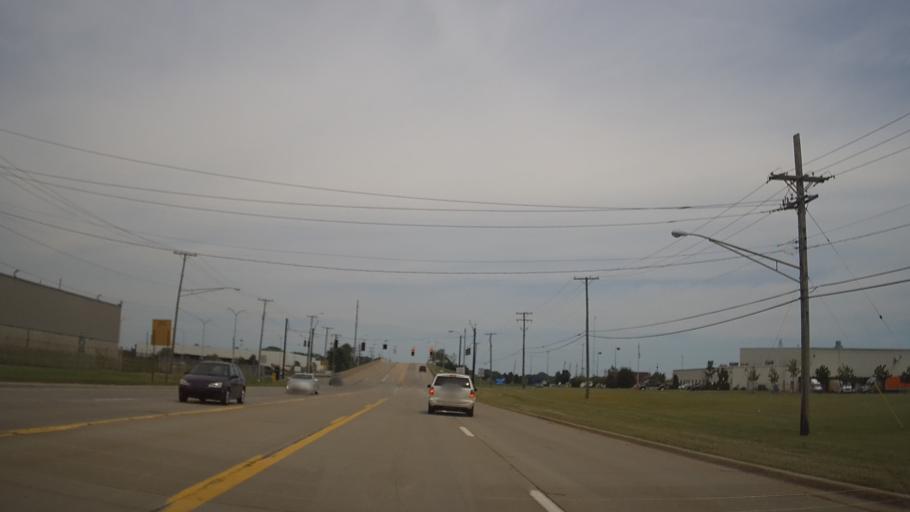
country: US
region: Michigan
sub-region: Macomb County
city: Sterling Heights
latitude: 42.5799
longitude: -83.0450
